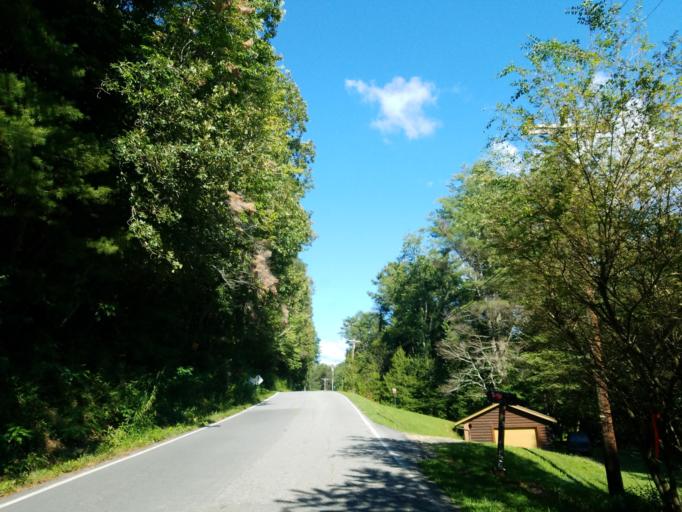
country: US
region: Georgia
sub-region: Fannin County
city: Blue Ridge
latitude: 34.7589
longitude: -84.2139
